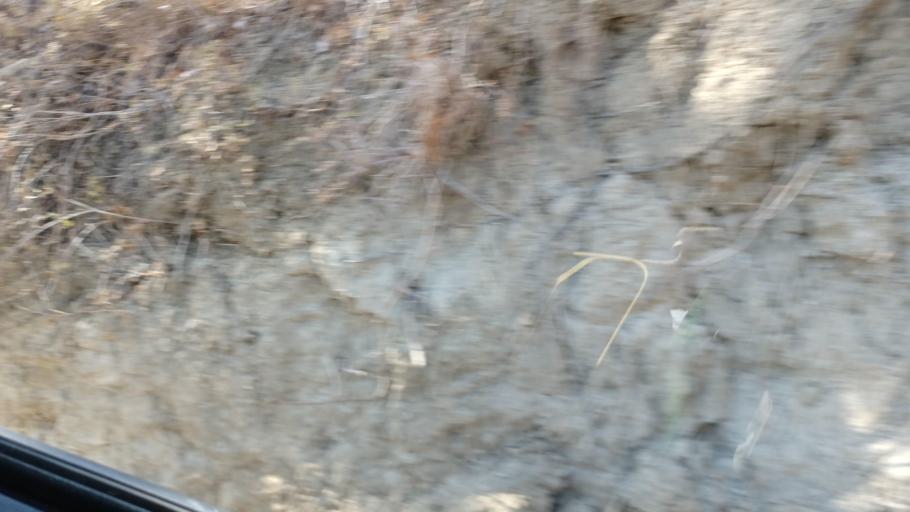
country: CY
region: Pafos
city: Tala
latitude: 34.9378
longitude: 32.4769
